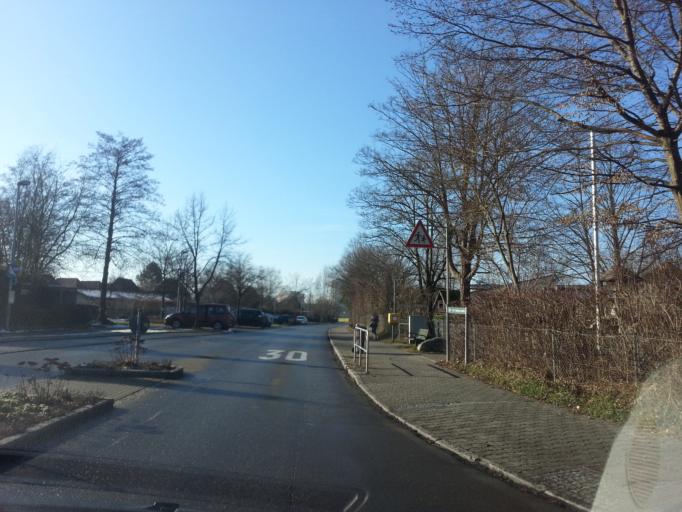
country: DE
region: Baden-Wuerttemberg
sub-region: Tuebingen Region
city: Immenstaad am Bodensee
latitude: 47.6719
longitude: 9.3804
